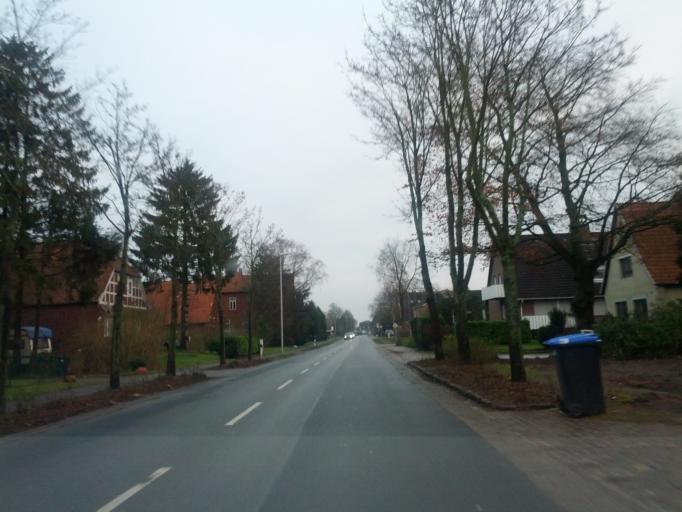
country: DE
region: Lower Saxony
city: Jork
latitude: 53.5280
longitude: 9.7010
